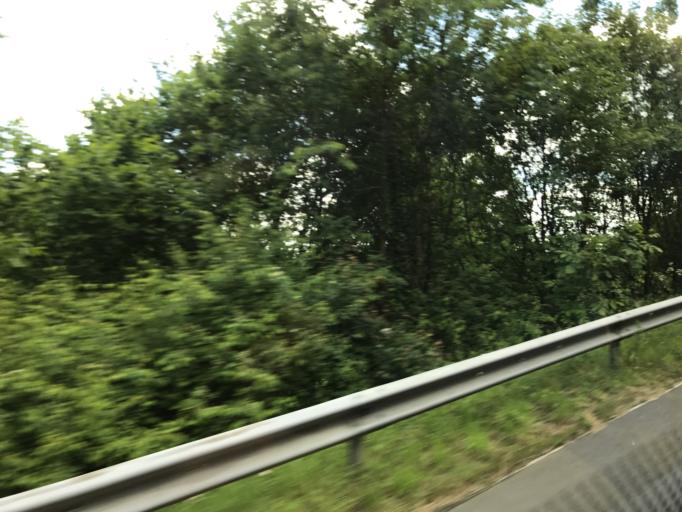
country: DE
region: Hesse
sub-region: Regierungsbezirk Darmstadt
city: Eltville
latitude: 50.0562
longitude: 8.1179
